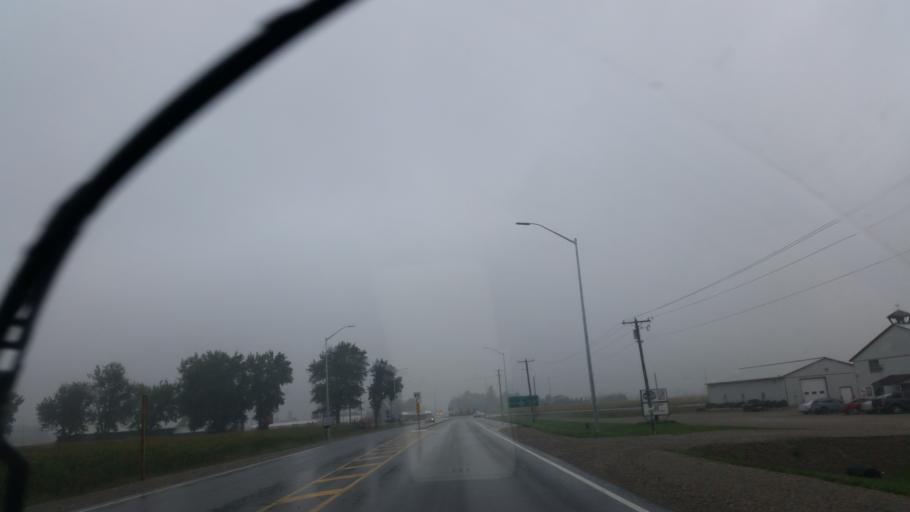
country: CA
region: Ontario
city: Stratford
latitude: 43.3264
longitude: -81.0208
